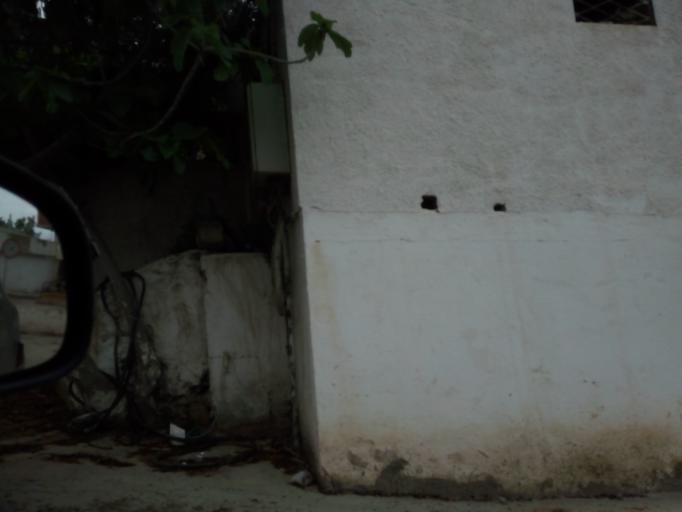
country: DZ
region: Medea
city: Medea
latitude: 36.2782
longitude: 2.7762
